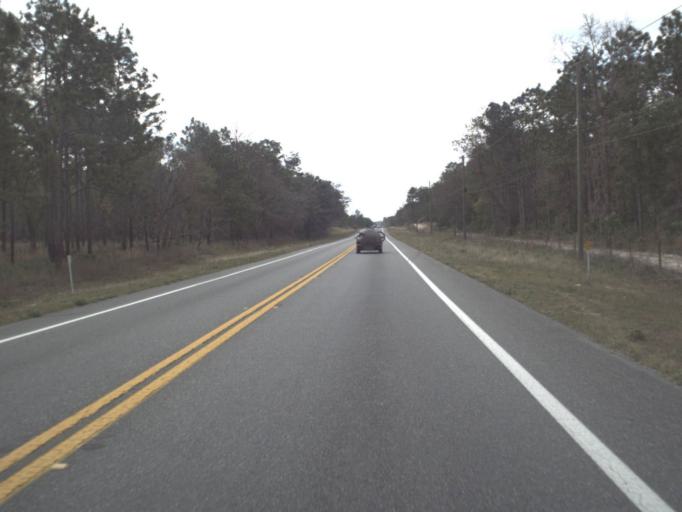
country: US
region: Florida
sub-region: Marion County
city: Ocala
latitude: 29.2519
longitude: -82.0659
